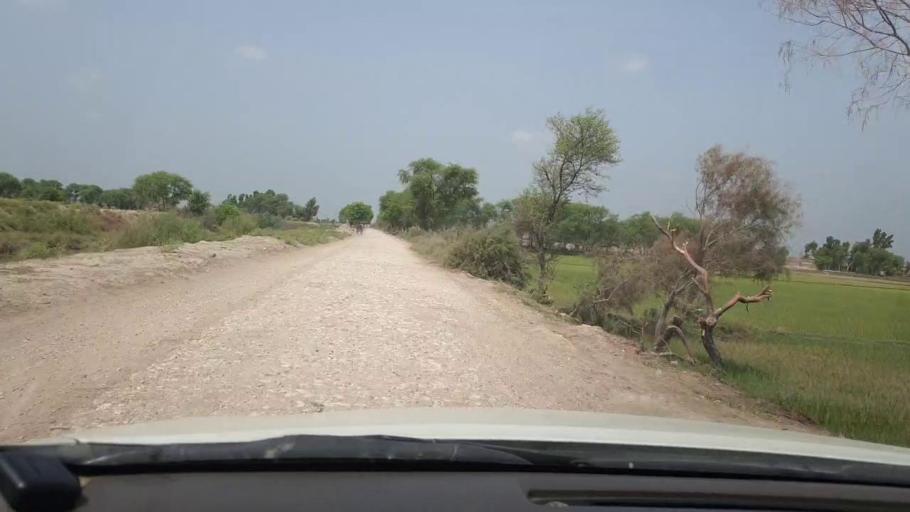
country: PK
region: Sindh
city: Garhi Yasin
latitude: 28.0131
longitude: 68.5372
